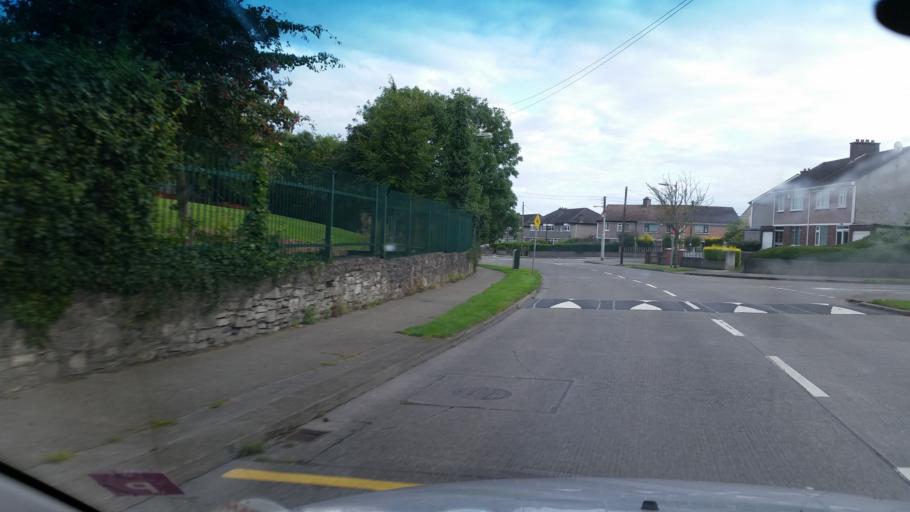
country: IE
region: Leinster
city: Glasnevin
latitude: 53.3852
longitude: -6.2784
